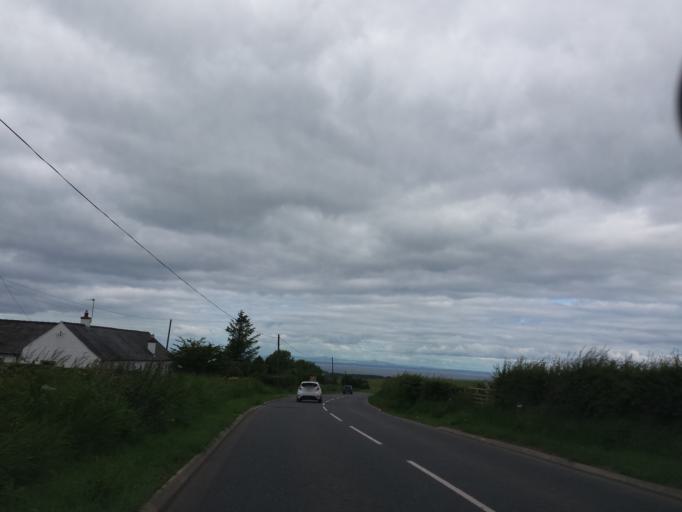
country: GB
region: Scotland
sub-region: East Lothian
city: Haddington
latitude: 55.9772
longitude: -2.8087
